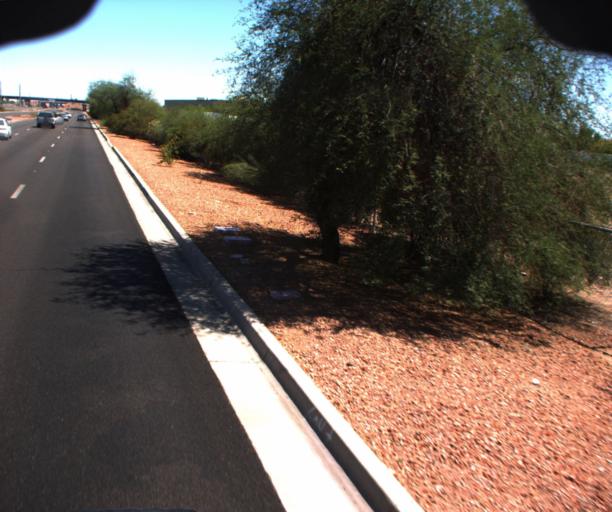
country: US
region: Arizona
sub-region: Maricopa County
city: Peoria
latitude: 33.5709
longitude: -112.2252
